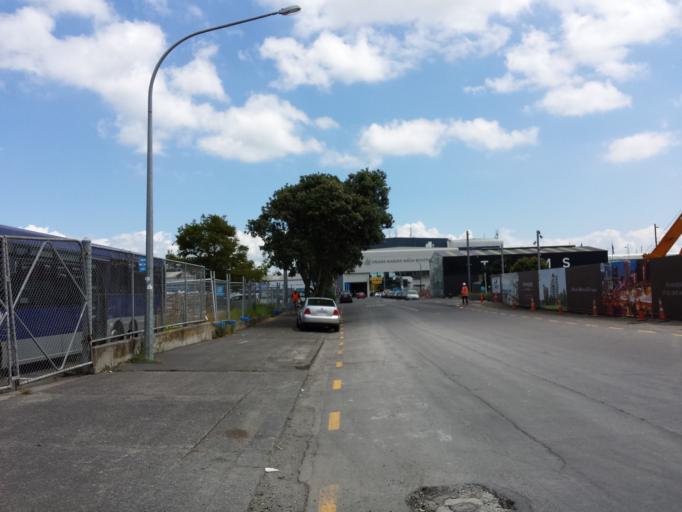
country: NZ
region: Auckland
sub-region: Auckland
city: Auckland
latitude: -36.8433
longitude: 174.7558
